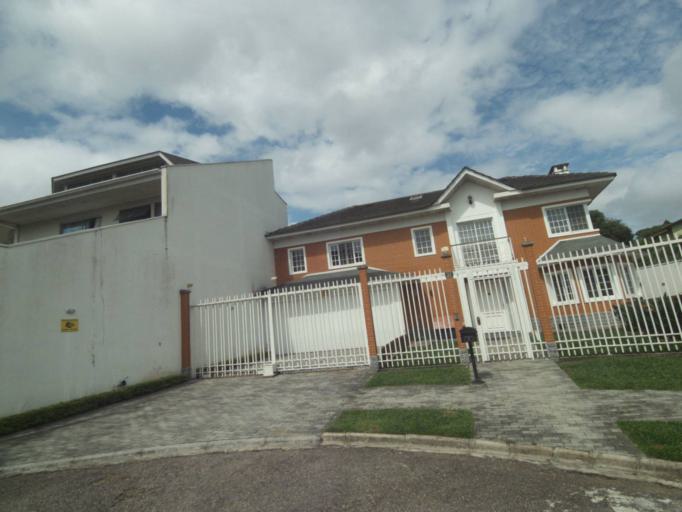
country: BR
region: Parana
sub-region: Curitiba
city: Curitiba
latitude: -25.3812
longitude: -49.2816
